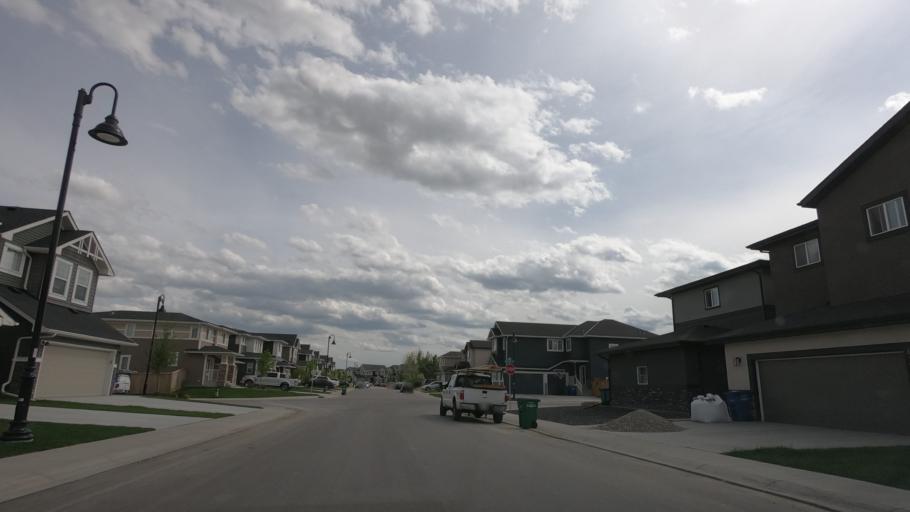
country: CA
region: Alberta
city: Airdrie
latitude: 51.2766
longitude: -114.0426
